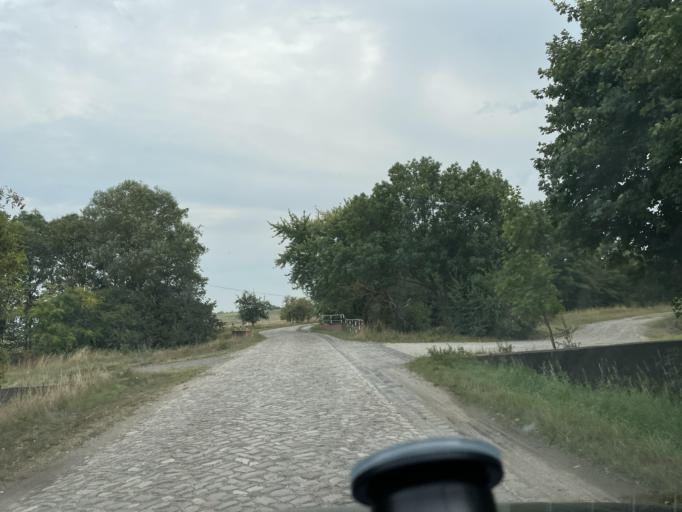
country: DE
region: Saxony-Anhalt
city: Brumby
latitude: 51.9107
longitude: 11.7413
